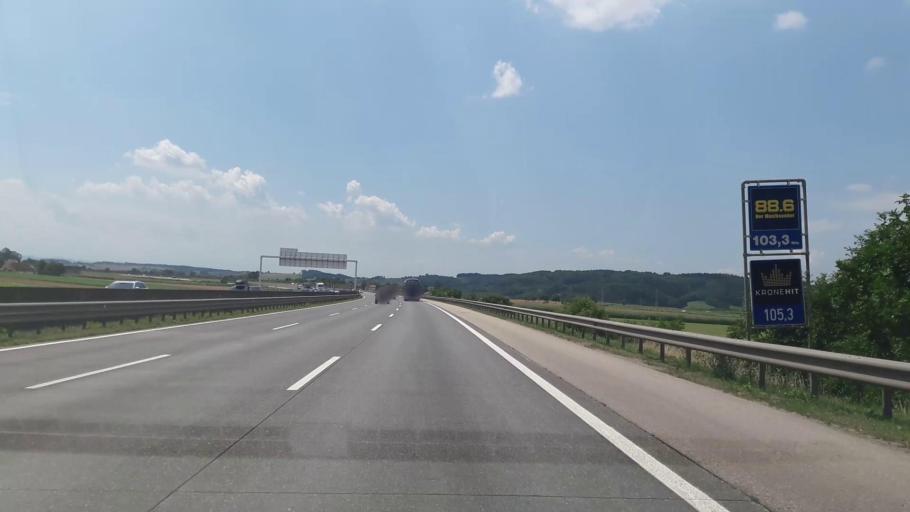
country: AT
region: Lower Austria
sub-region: Politischer Bezirk Melk
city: Pochlarn
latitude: 48.1920
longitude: 15.2068
